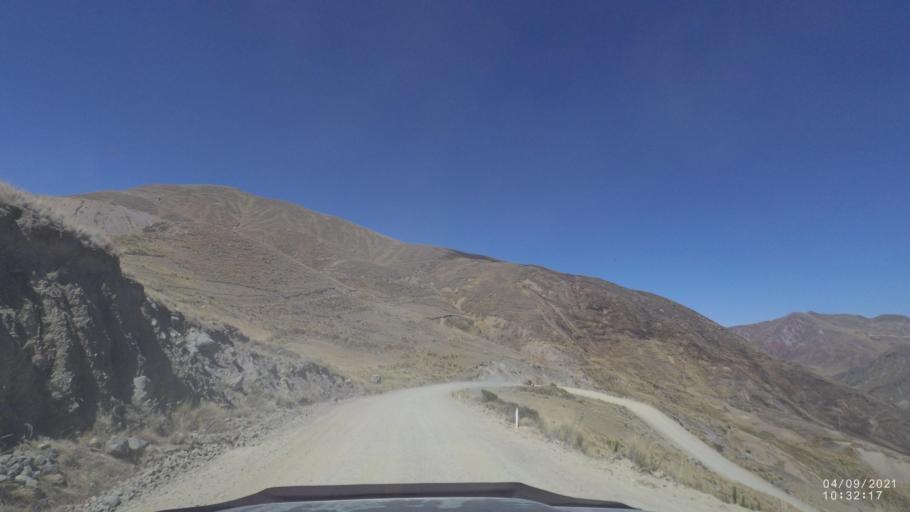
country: BO
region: Cochabamba
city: Sipe Sipe
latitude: -17.2987
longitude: -66.4471
